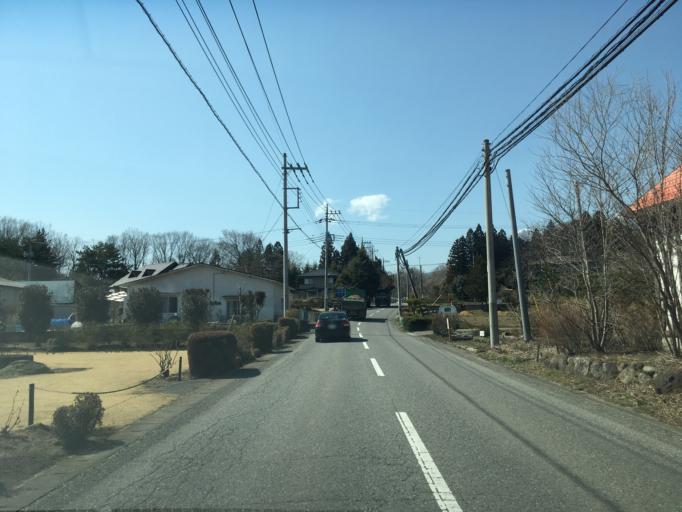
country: JP
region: Tochigi
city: Kuroiso
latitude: 37.0579
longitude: 140.0098
